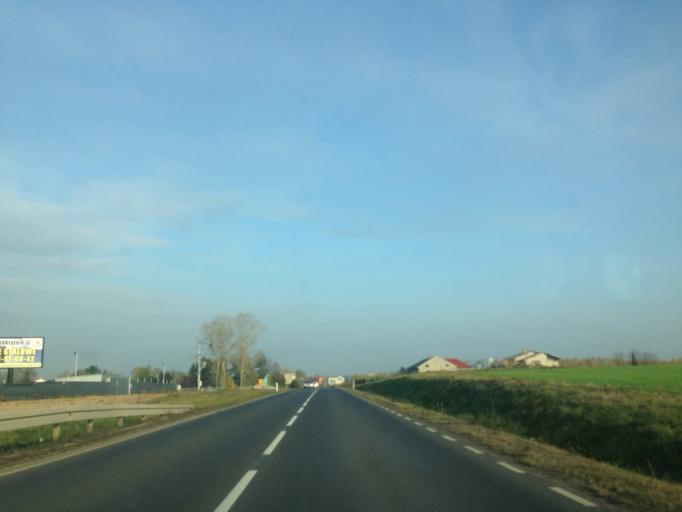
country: PL
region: Kujawsko-Pomorskie
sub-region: Powiat wabrzeski
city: Wabrzezno
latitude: 53.2679
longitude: 18.9668
